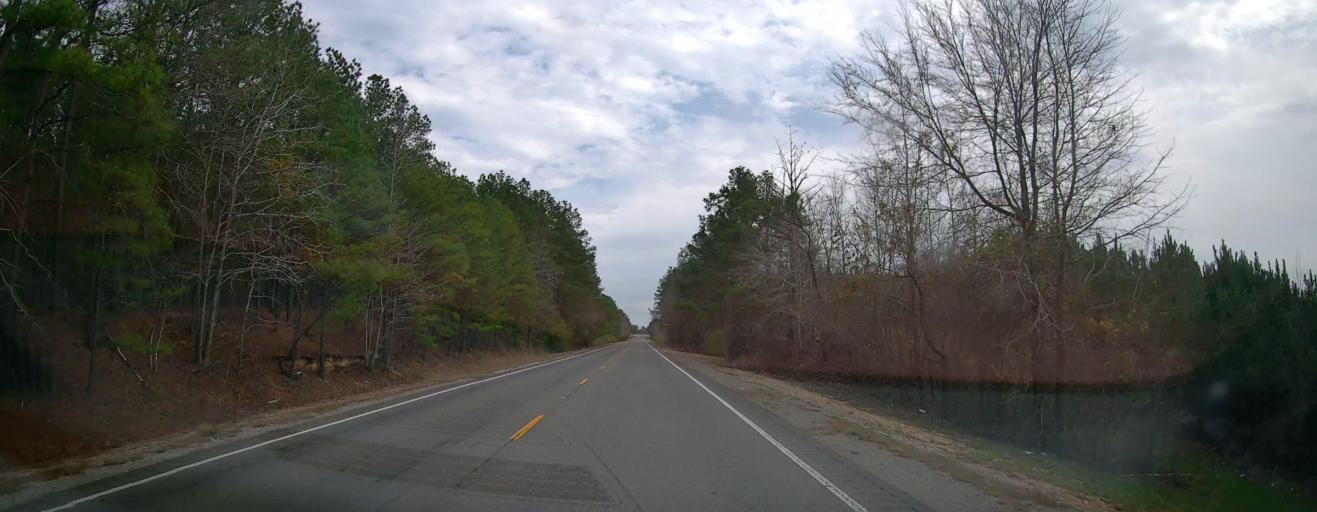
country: US
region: Alabama
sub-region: Marion County
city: Guin
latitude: 34.0448
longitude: -87.9587
